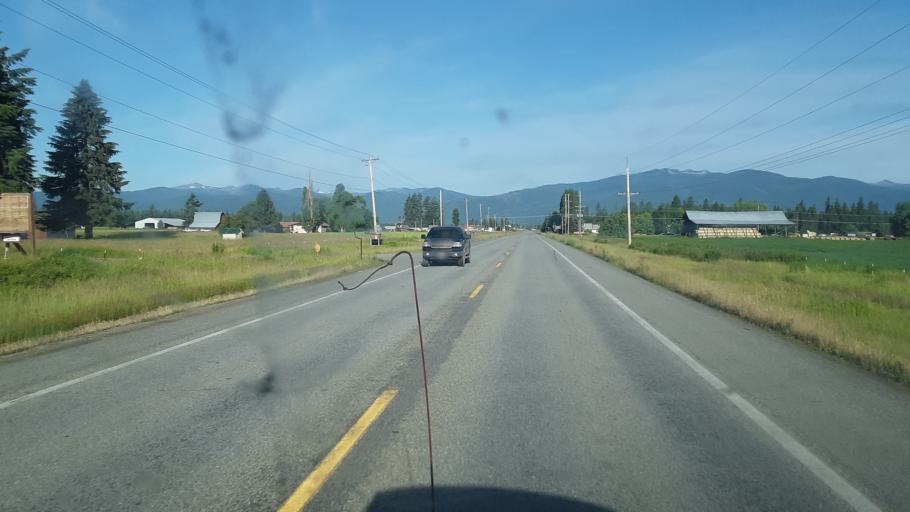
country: US
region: Idaho
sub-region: Boundary County
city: Bonners Ferry
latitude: 48.7315
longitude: -116.2714
